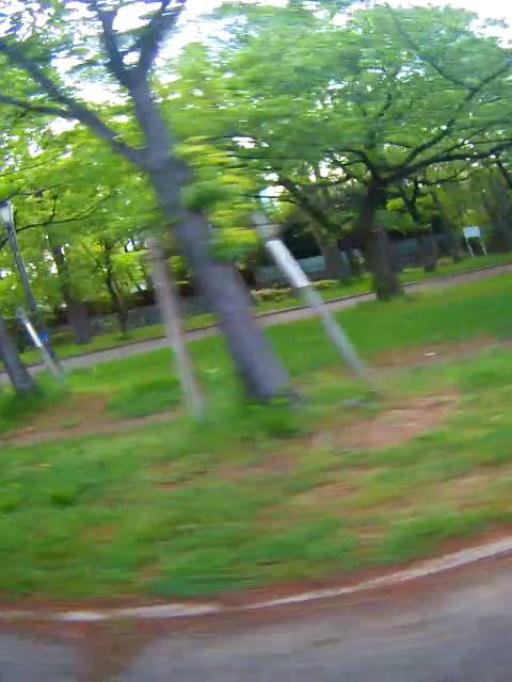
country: JP
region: Osaka
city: Osaka-shi
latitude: 34.7109
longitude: 135.5213
